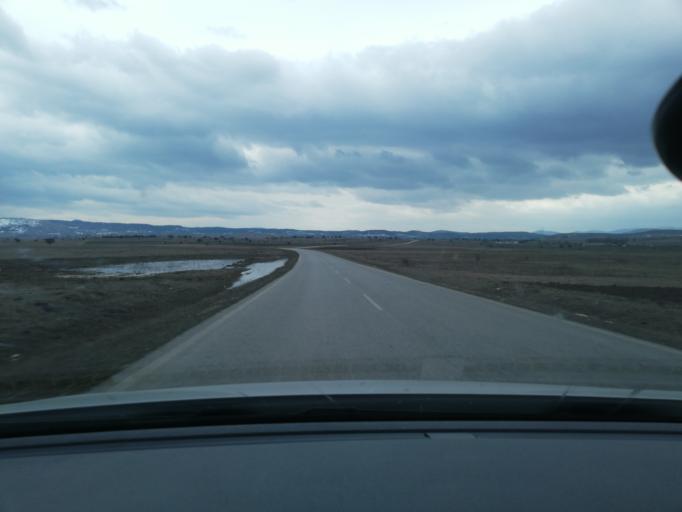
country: TR
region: Bolu
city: Gerede
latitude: 40.7202
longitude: 32.2233
